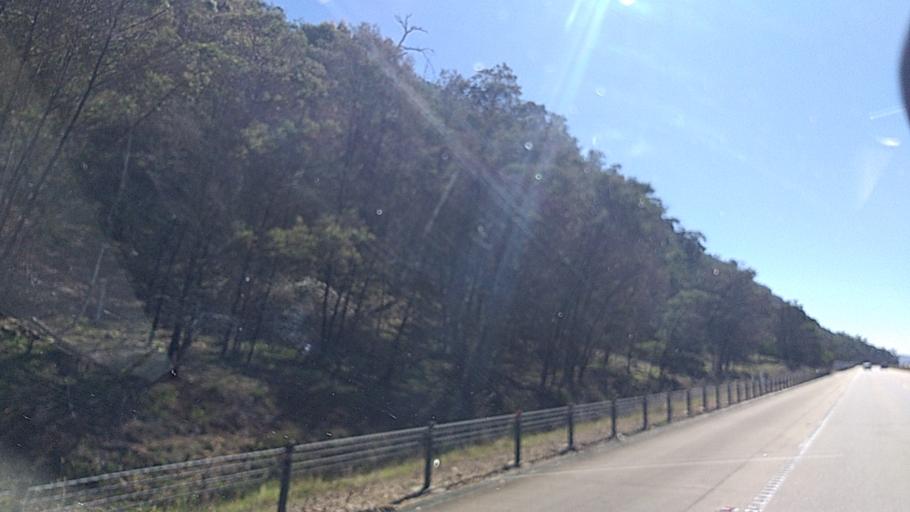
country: AU
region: New South Wales
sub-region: Yass Valley
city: Gundaroo
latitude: -35.0550
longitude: 149.3750
